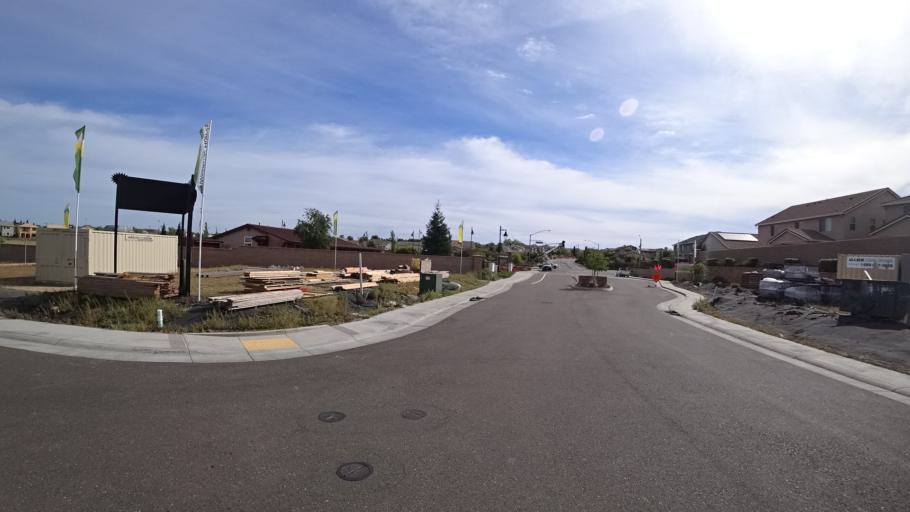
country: US
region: California
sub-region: Placer County
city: Rocklin
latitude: 38.8260
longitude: -121.2868
